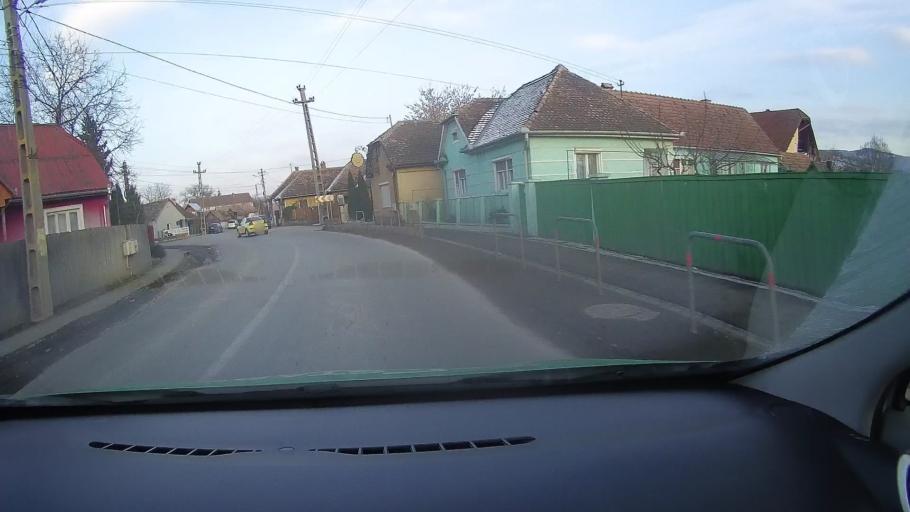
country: RO
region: Harghita
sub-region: Oras Cristuru Secuiesc
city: Cristuru Secuiesc
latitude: 46.2824
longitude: 25.0232
